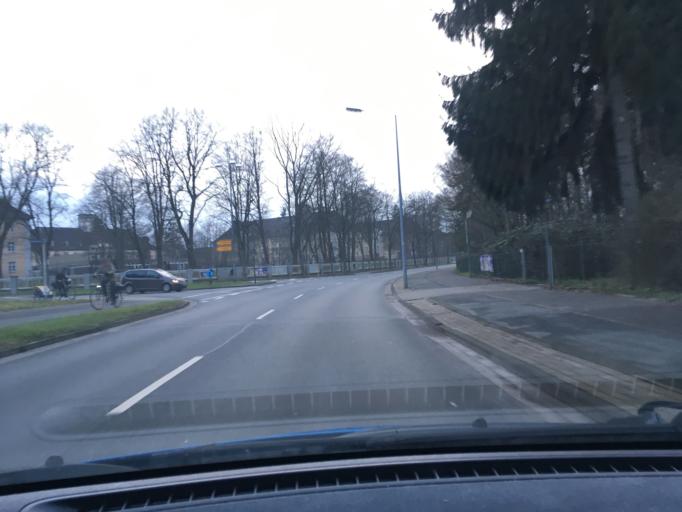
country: DE
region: Lower Saxony
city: Celle
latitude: 52.6422
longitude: 10.0923
